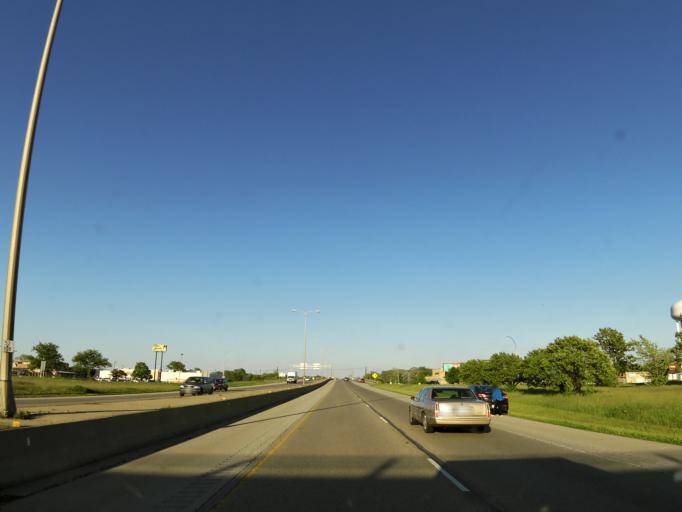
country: US
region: Illinois
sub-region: Champaign County
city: Champaign
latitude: 40.1347
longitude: -88.2432
